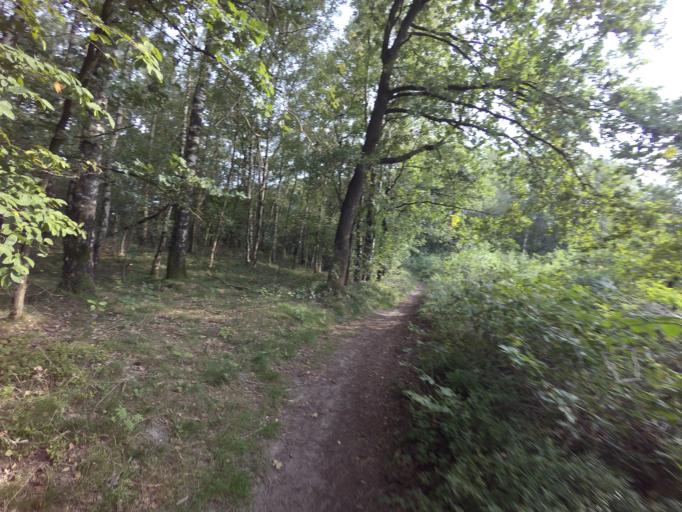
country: DE
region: Lower Saxony
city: Getelo
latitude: 52.4592
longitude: 6.8542
